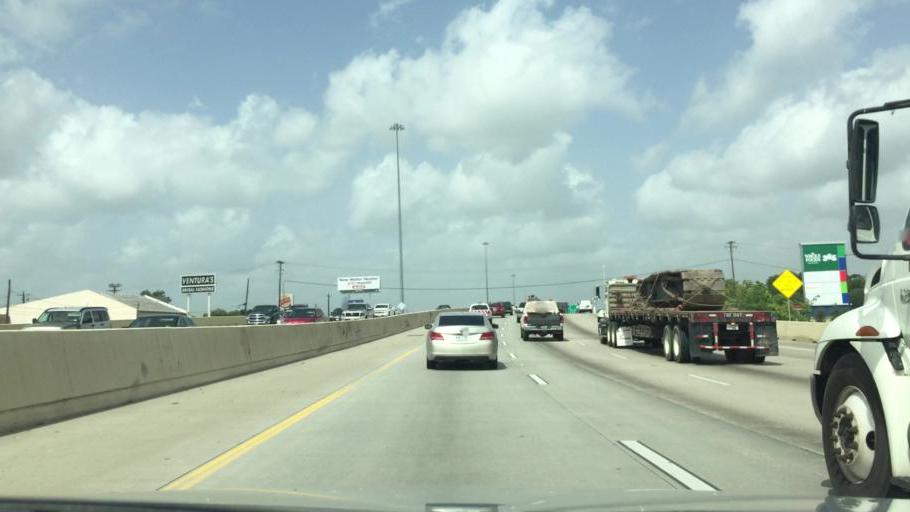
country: US
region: Texas
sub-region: Harris County
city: Houston
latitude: 29.8136
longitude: -95.3981
